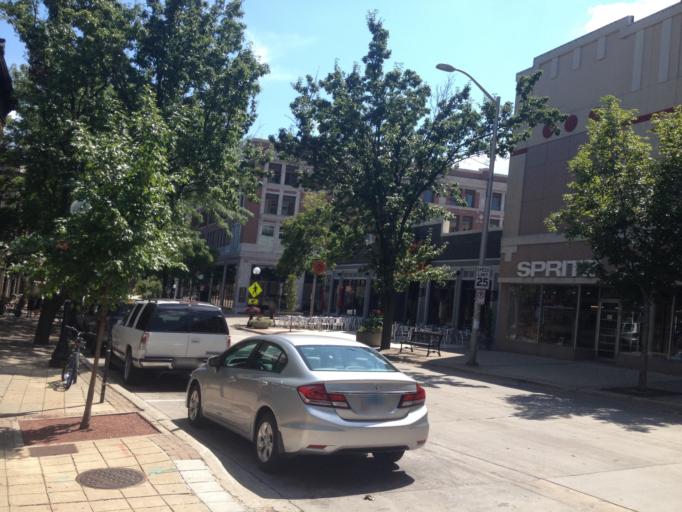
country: US
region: Illinois
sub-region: Champaign County
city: Champaign
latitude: 40.1178
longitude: -88.2435
